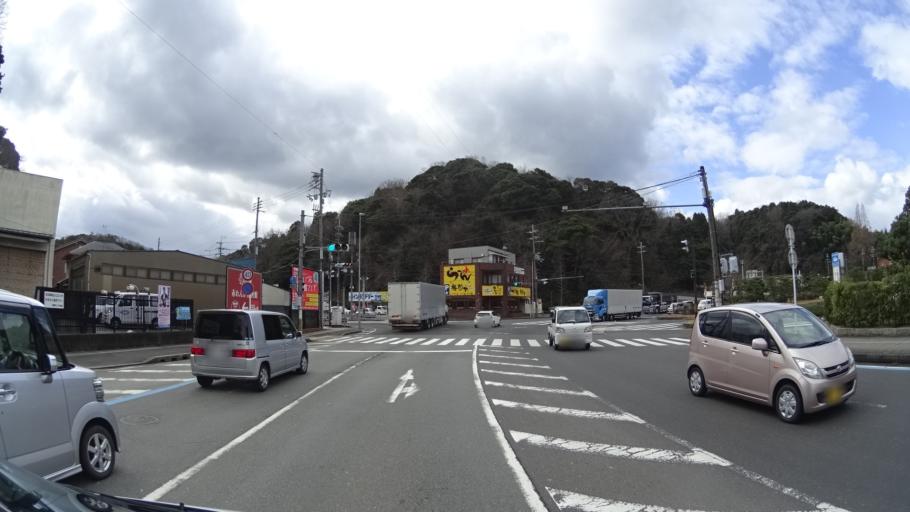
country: JP
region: Kyoto
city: Maizuru
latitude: 35.4744
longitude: 135.3868
